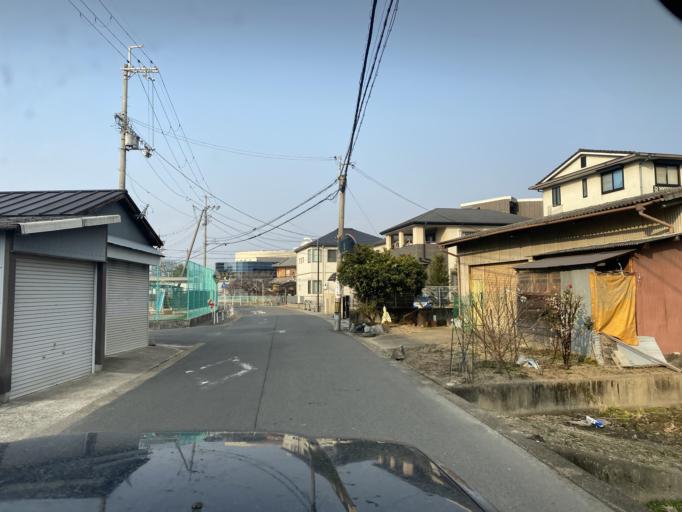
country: JP
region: Kyoto
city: Yawata
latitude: 34.8797
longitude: 135.7530
